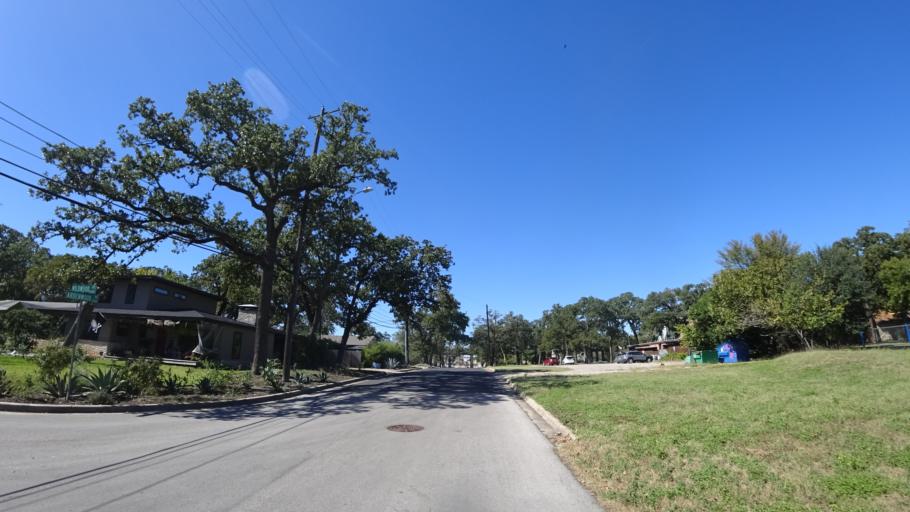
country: US
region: Texas
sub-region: Travis County
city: Austin
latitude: 30.2991
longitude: -97.7146
